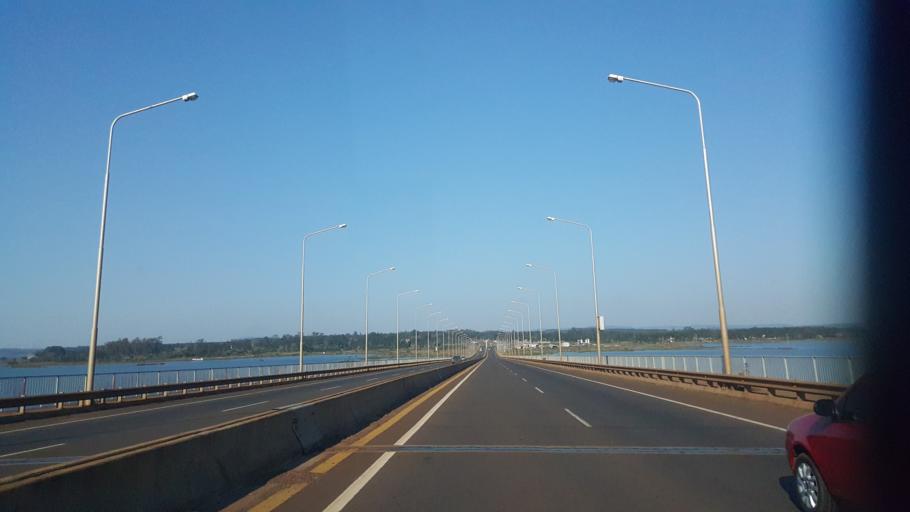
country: AR
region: Misiones
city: Garupa
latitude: -27.4626
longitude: -55.8172
